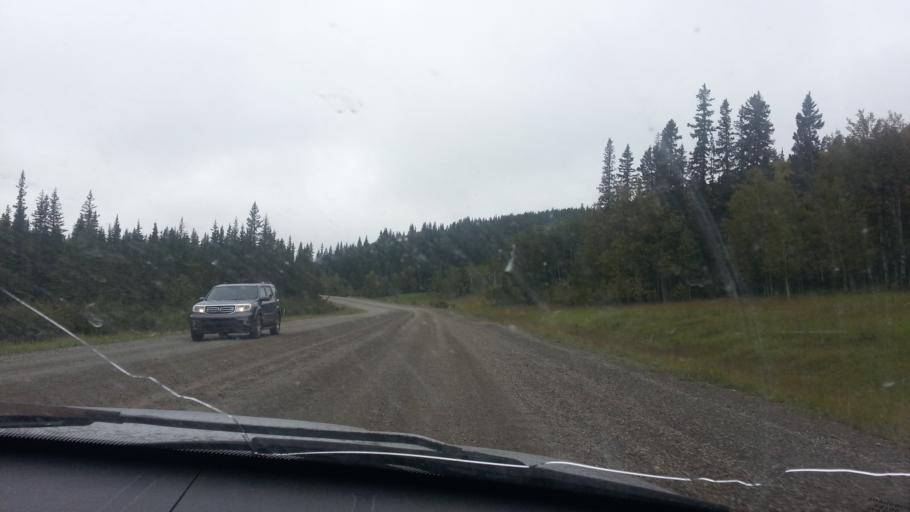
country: CA
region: Alberta
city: Cochrane
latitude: 51.0401
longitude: -114.7385
